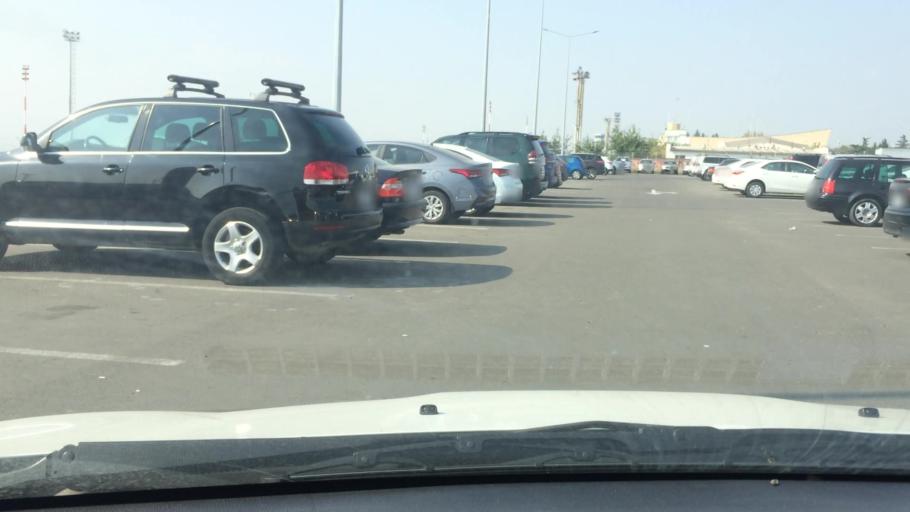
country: GE
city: Didi Lilo
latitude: 41.6709
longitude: 44.9626
